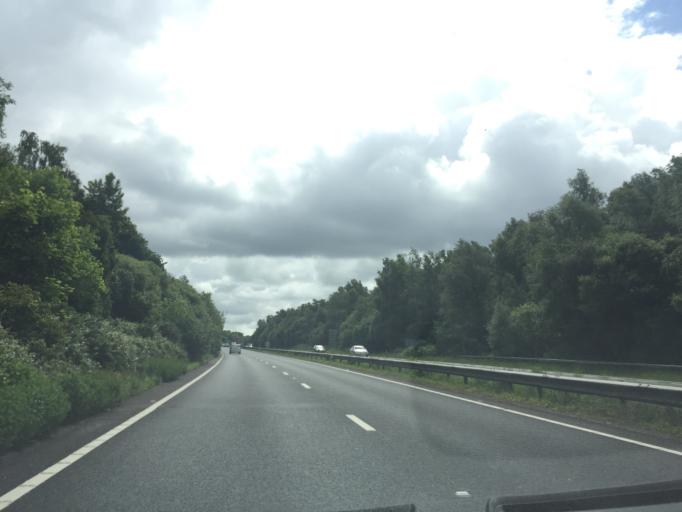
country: GB
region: England
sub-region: Dorset
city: Ferndown
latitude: 50.8152
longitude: -1.8829
